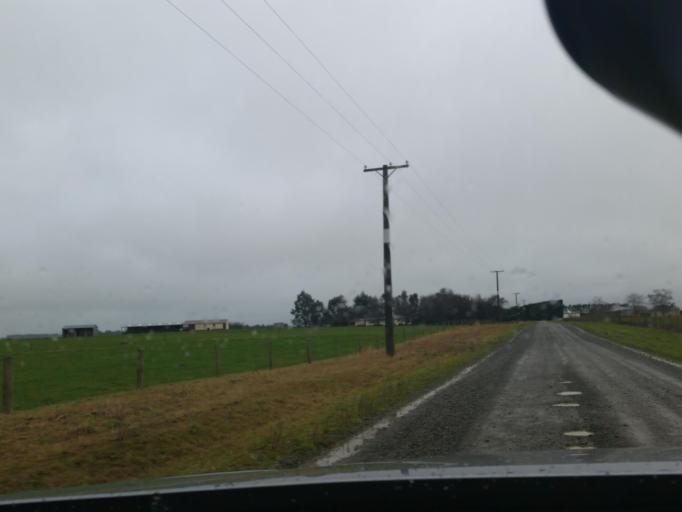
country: NZ
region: Southland
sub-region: Southland District
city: Winton
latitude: -46.1954
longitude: 168.2495
